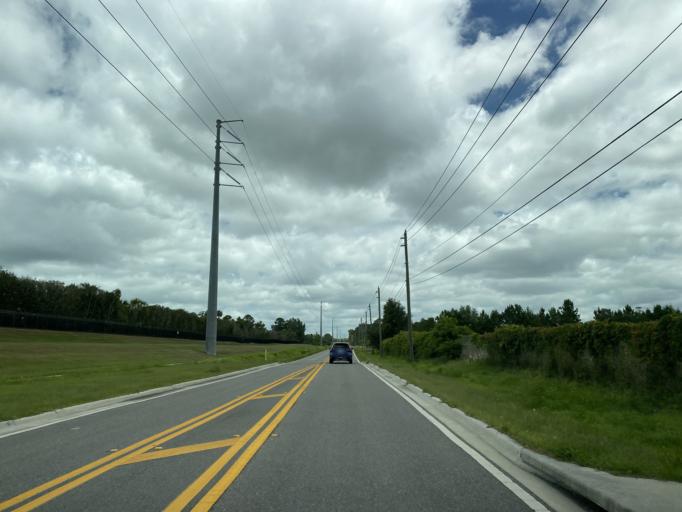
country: US
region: Florida
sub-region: Seminole County
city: Lake Mary
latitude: 28.8215
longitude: -81.3393
